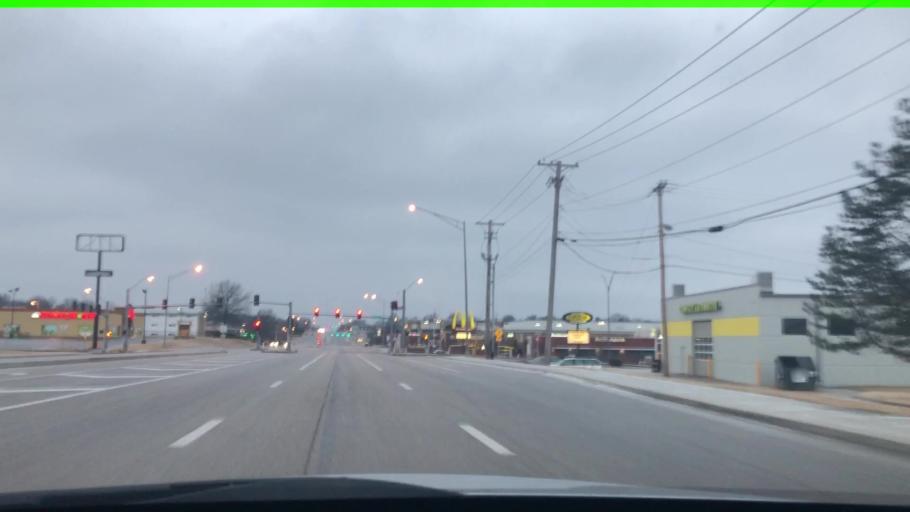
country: US
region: Missouri
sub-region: Boone County
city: Columbia
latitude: 38.9622
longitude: -92.3714
